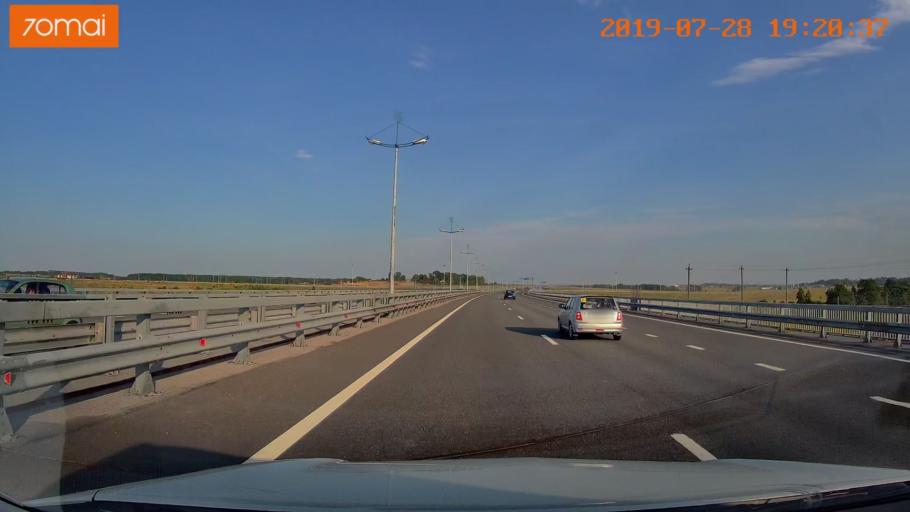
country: RU
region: Kaliningrad
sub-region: Zelenogradskiy Rayon
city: Zelenogradsk
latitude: 54.9137
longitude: 20.4900
